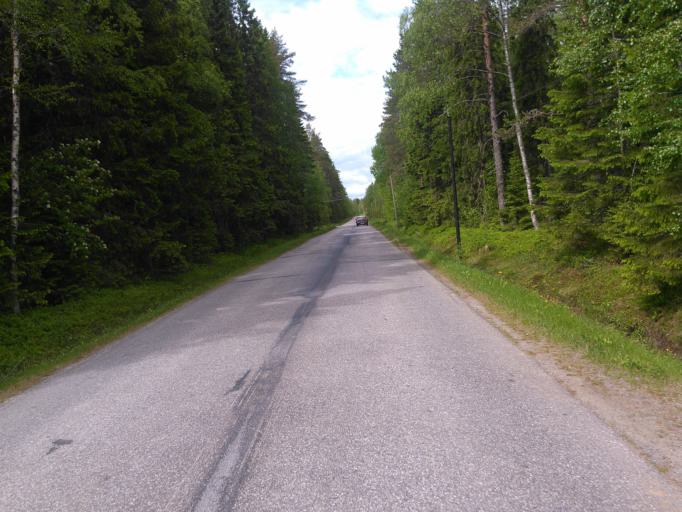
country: SE
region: Vaesterbotten
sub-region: Umea Kommun
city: Ersmark
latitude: 63.8704
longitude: 20.3328
